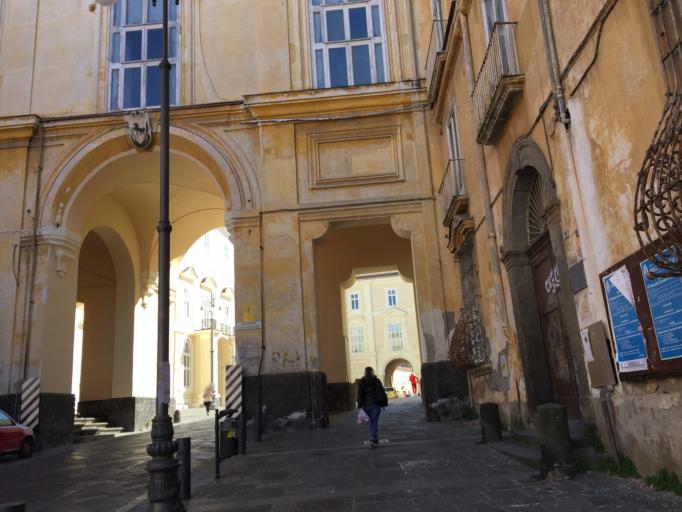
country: IT
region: Campania
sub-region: Provincia di Napoli
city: Portici
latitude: 40.8117
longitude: 14.3422
